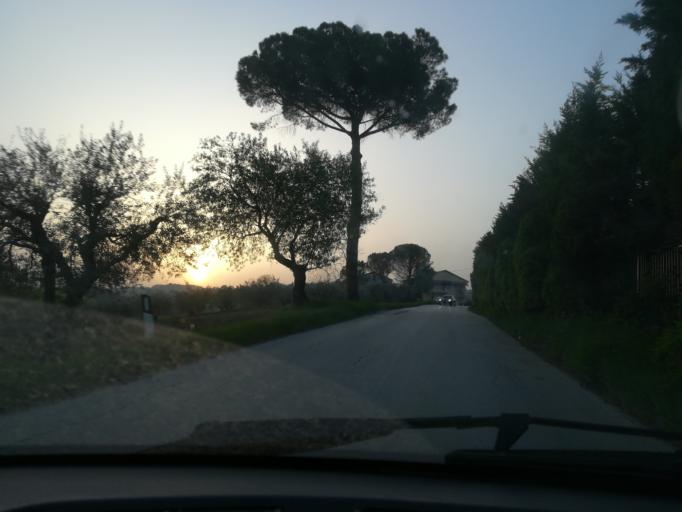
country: IT
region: The Marches
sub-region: Provincia di Macerata
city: Macerata
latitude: 43.2720
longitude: 13.4579
